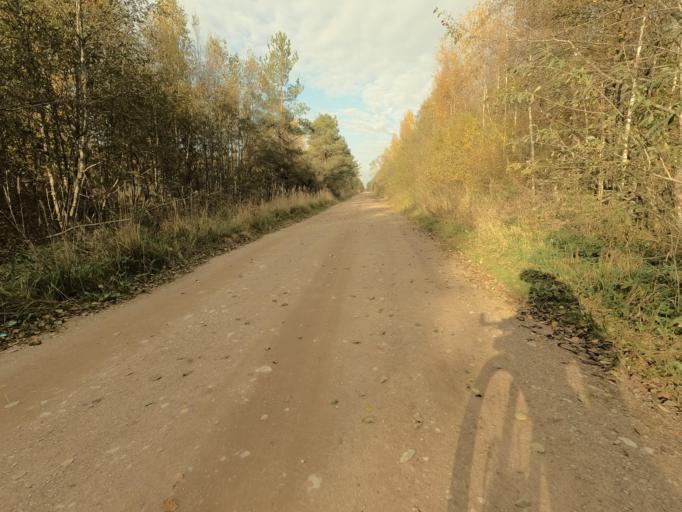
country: RU
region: Novgorod
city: Volkhovskiy
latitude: 58.8948
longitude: 31.0292
